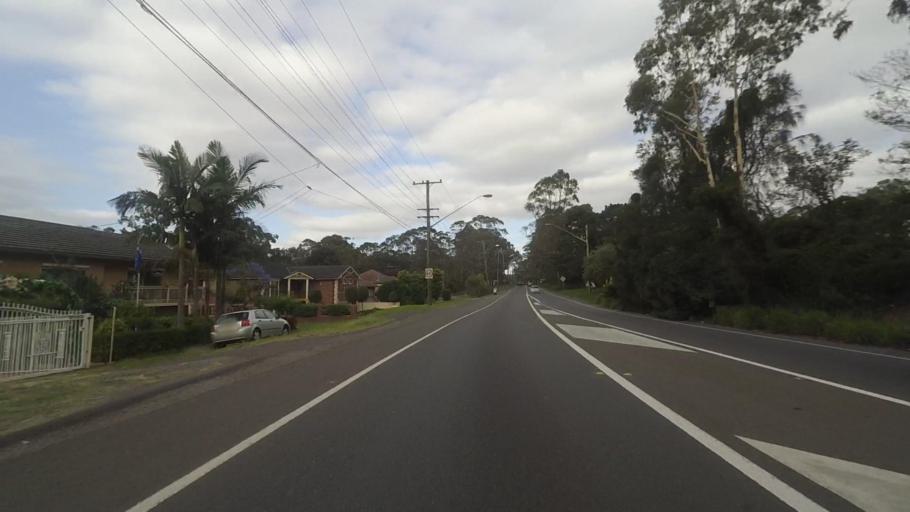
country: AU
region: New South Wales
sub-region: Bankstown
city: Milperra
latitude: -33.9105
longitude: 150.9772
